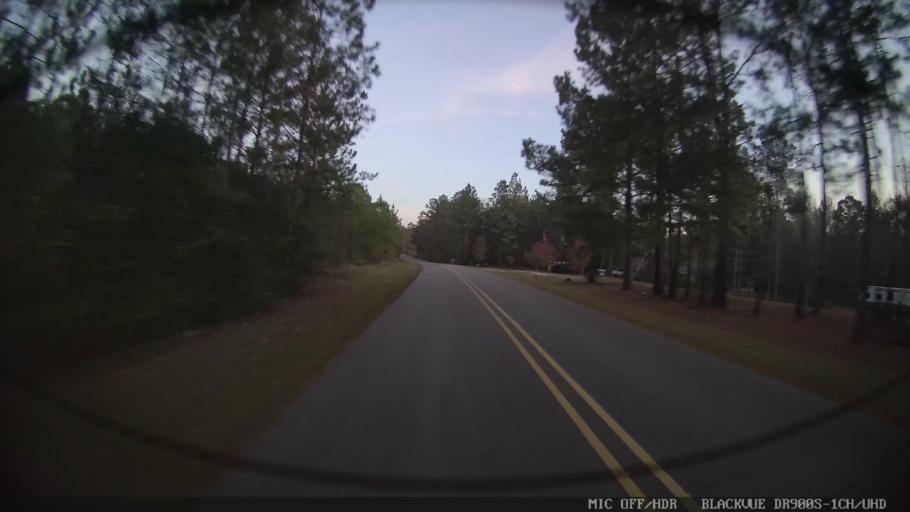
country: US
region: Mississippi
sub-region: Lamar County
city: Purvis
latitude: 31.0751
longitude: -89.2086
